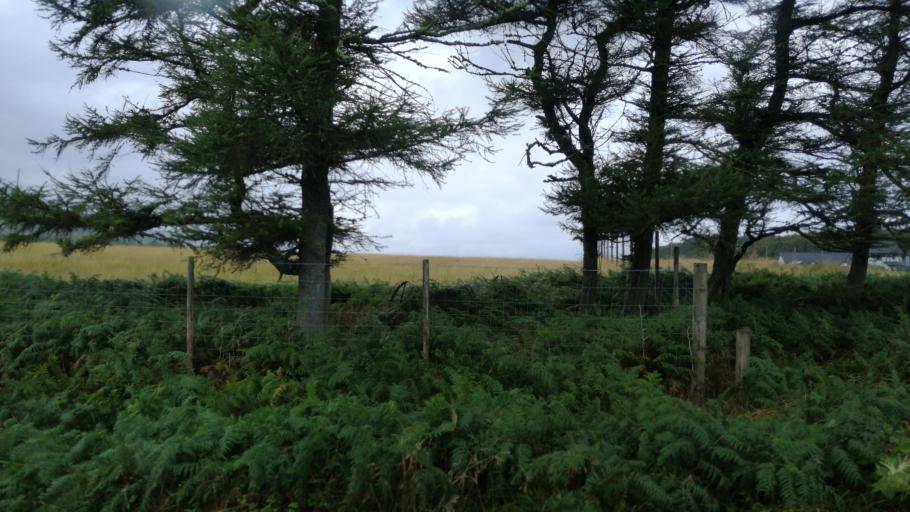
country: GB
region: Scotland
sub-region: Argyll and Bute
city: Isle Of Mull
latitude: 56.4782
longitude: -5.7154
